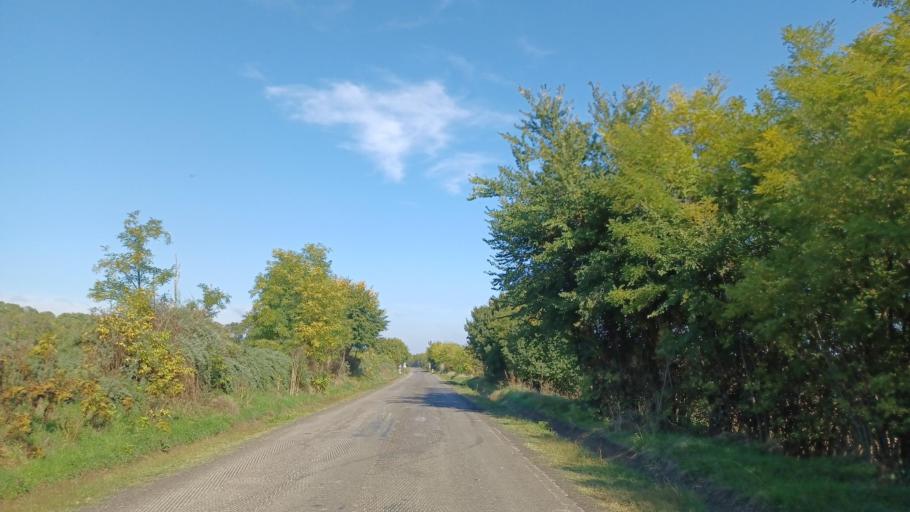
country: HU
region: Tolna
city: Nagydorog
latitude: 46.5935
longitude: 18.5959
